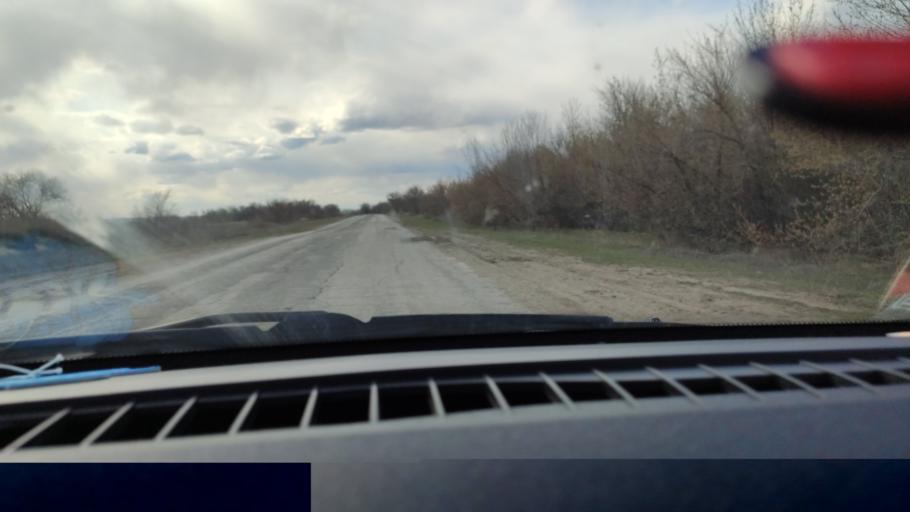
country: RU
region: Saratov
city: Rovnoye
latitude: 51.0447
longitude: 46.0582
